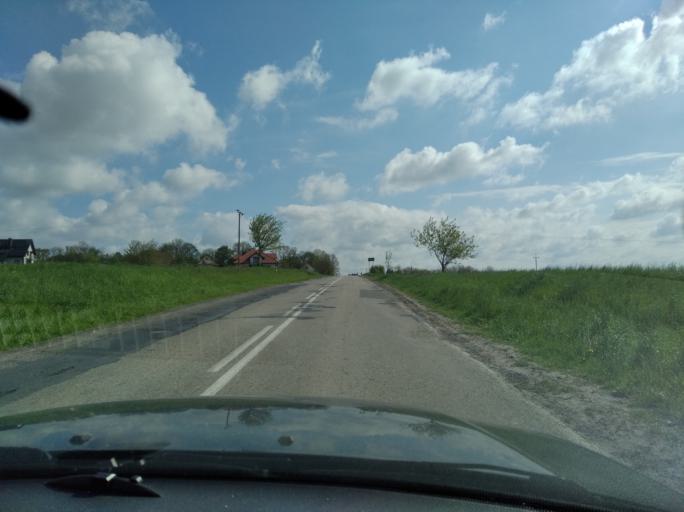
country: PL
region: Subcarpathian Voivodeship
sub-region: Powiat przeworski
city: Urzejowice
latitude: 50.0029
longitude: 22.4346
